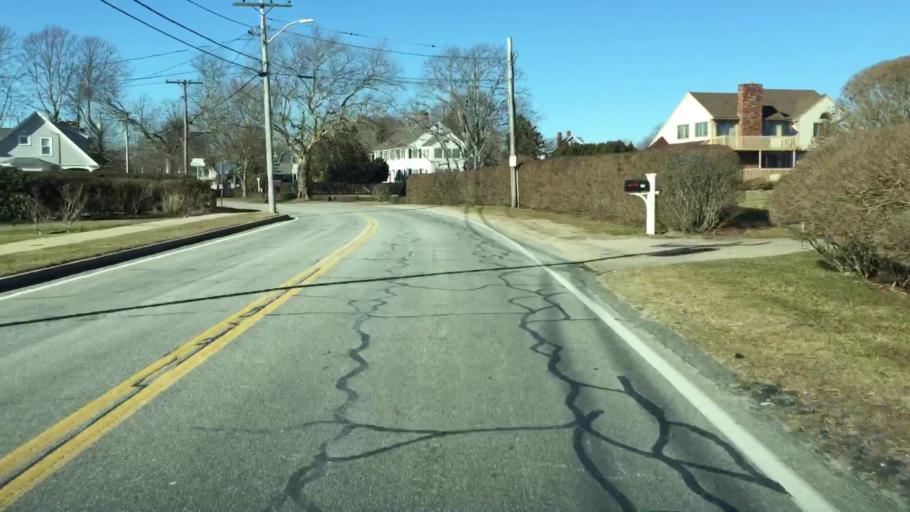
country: US
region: Massachusetts
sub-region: Barnstable County
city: Falmouth
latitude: 41.5446
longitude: -70.6080
